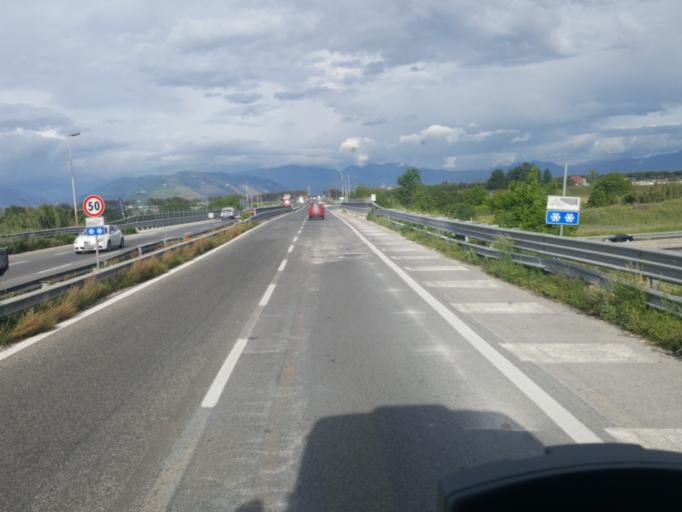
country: IT
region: Campania
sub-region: Provincia di Napoli
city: Pascarola
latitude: 40.9734
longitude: 14.3247
